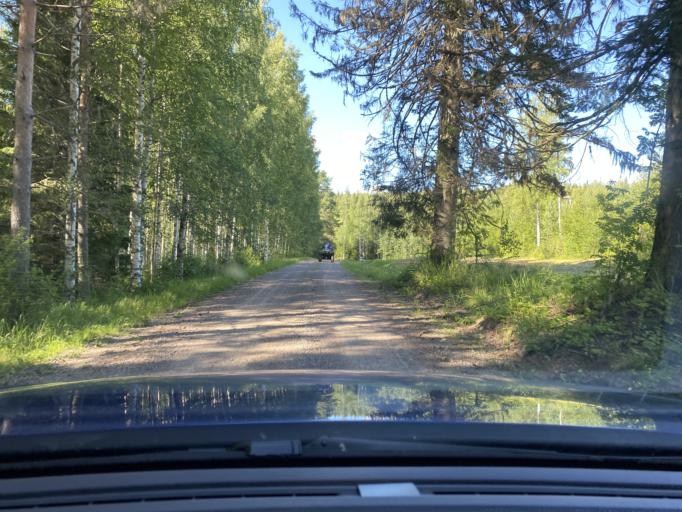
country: FI
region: Pirkanmaa
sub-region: Ylae-Pirkanmaa
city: Maenttae
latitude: 62.0170
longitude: 24.7418
